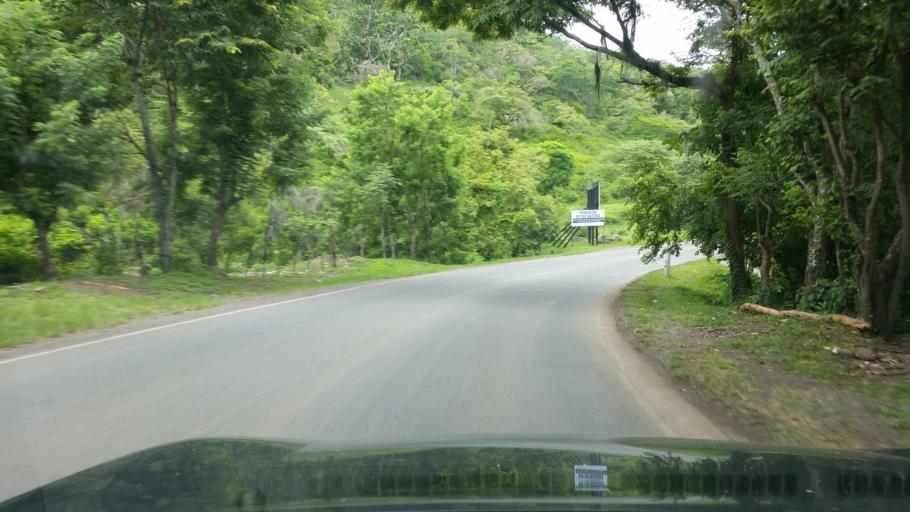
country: NI
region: Matagalpa
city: Matagalpa
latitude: 12.9420
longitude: -85.8938
